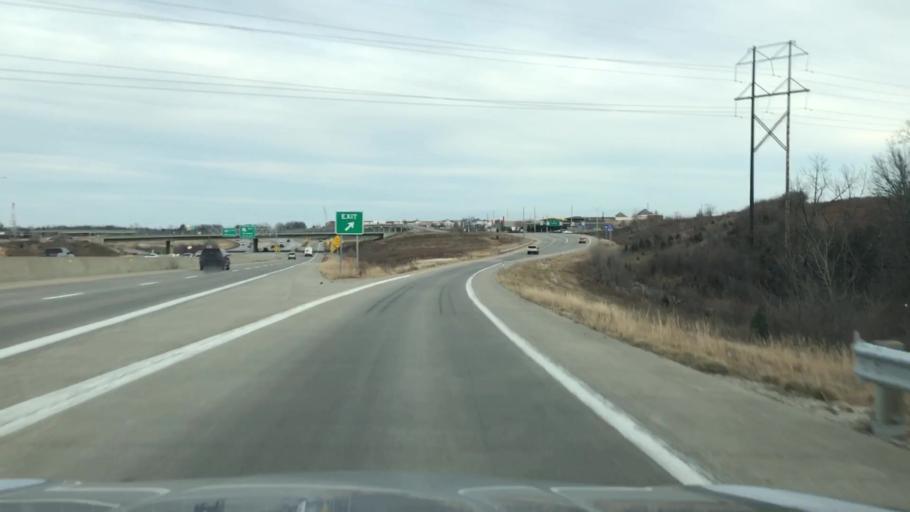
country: US
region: Missouri
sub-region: Jackson County
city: Lees Summit
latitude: 38.9339
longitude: -94.4166
